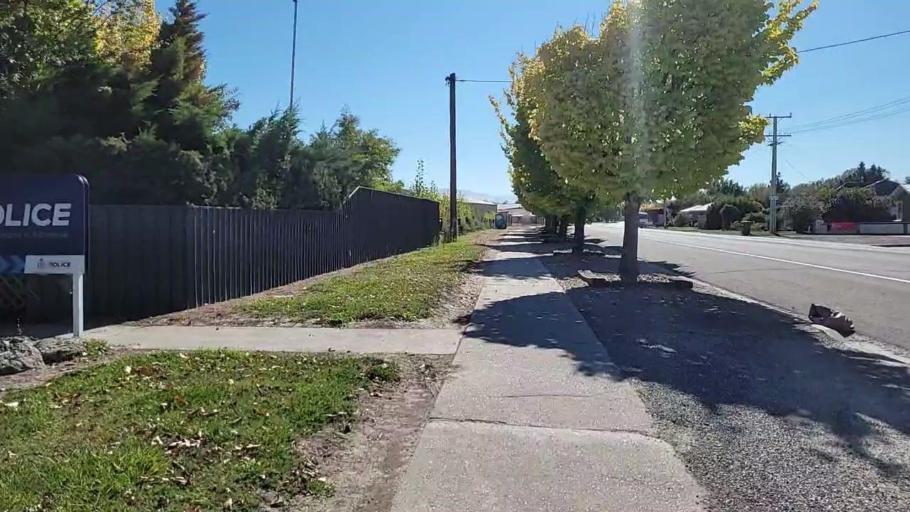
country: NZ
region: Otago
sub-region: Queenstown-Lakes District
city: Wanaka
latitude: -45.0992
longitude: 169.5972
